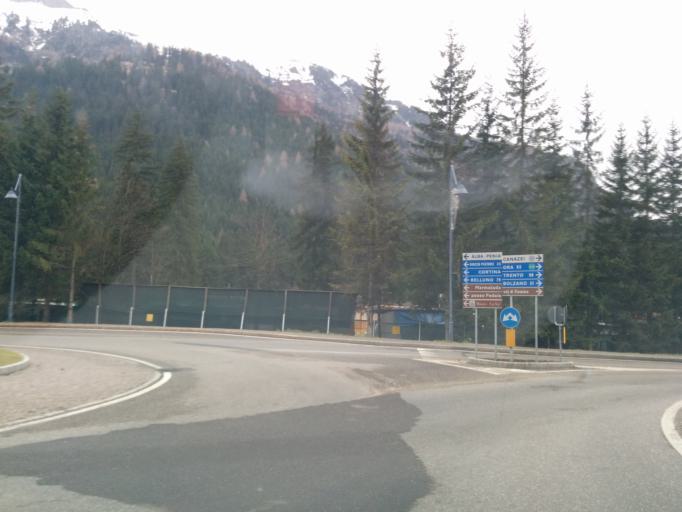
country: IT
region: Trentino-Alto Adige
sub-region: Provincia di Trento
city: Canazei
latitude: 46.4727
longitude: 11.7770
